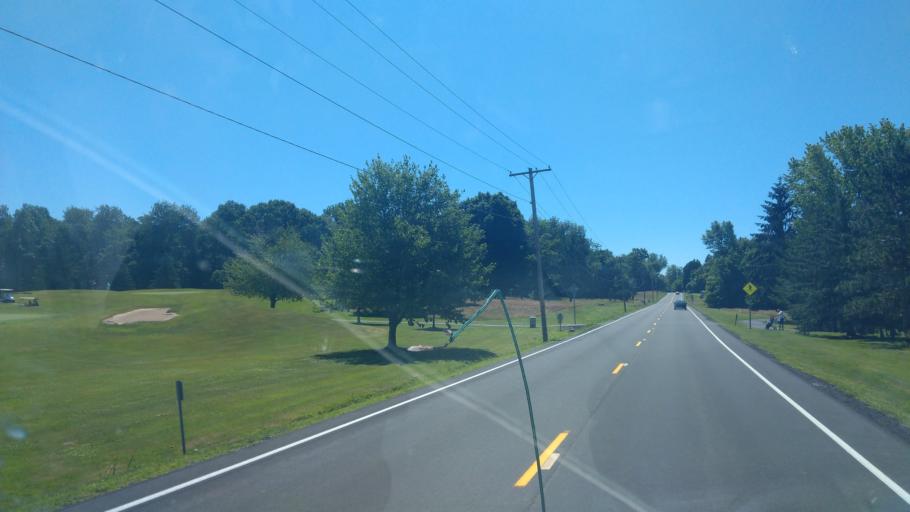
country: US
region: New York
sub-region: Wayne County
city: Sodus
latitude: 43.2474
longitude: -76.9900
